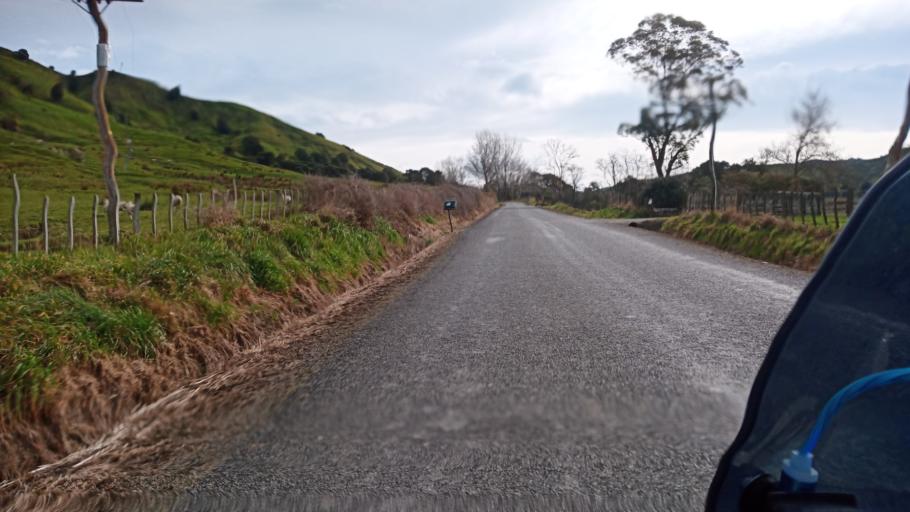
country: NZ
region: Hawke's Bay
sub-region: Wairoa District
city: Wairoa
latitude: -38.8050
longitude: 177.4744
